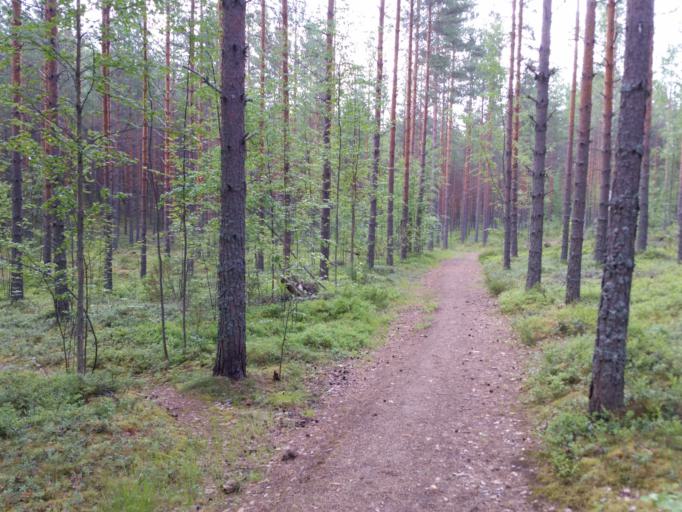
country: FI
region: Southern Savonia
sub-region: Savonlinna
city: Sulkava
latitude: 61.7620
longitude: 28.4338
